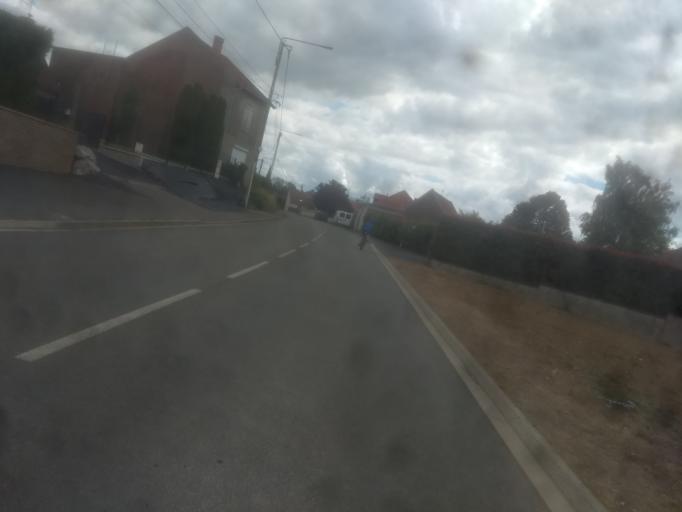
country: FR
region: Nord-Pas-de-Calais
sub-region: Departement du Pas-de-Calais
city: Agny
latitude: 50.2124
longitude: 2.7772
